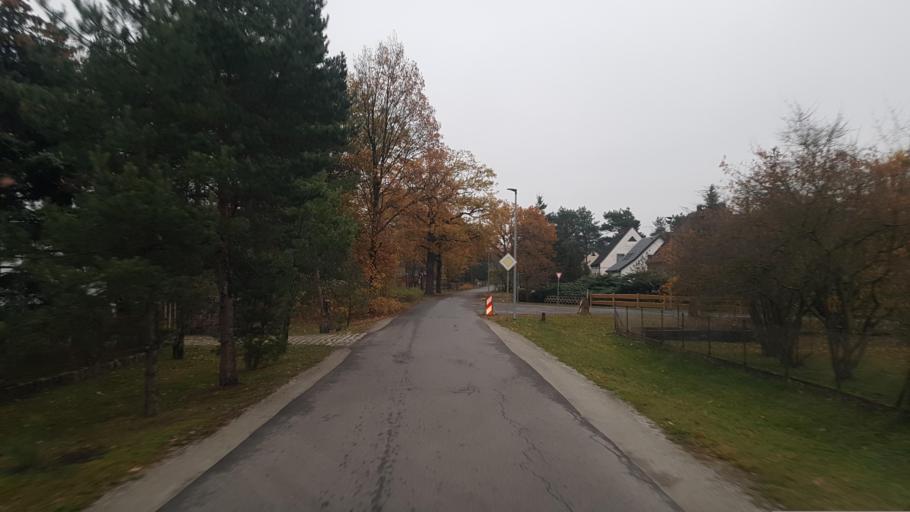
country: DE
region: Brandenburg
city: Ruhland
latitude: 51.4515
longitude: 13.8679
